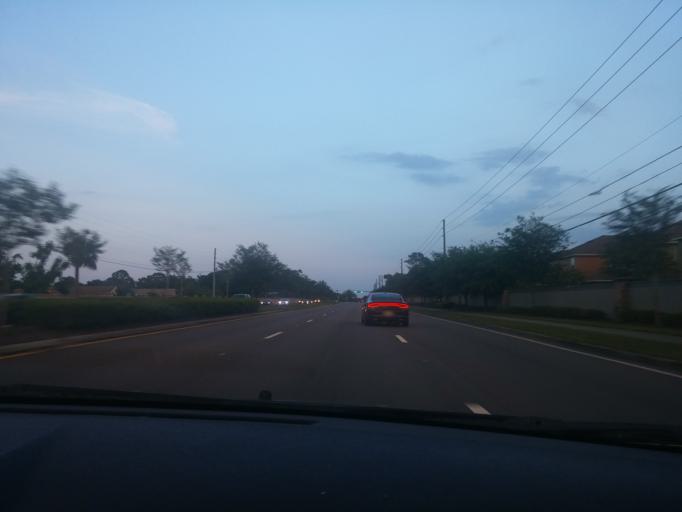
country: US
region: Florida
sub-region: Seminole County
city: Goldenrod
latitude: 28.6477
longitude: -81.2575
